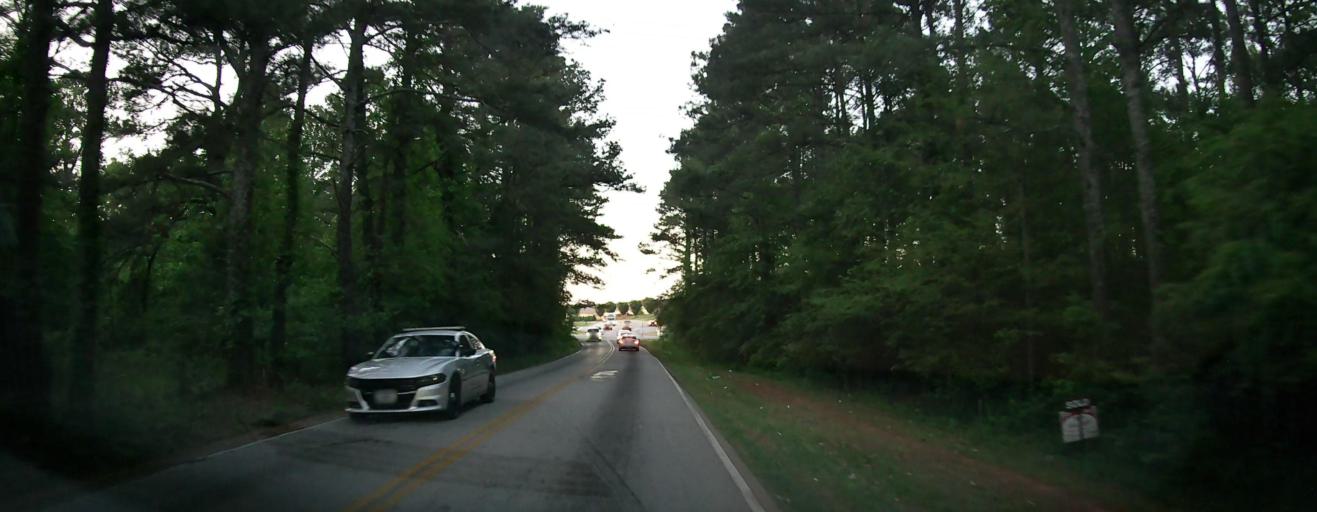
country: US
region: Georgia
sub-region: Henry County
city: McDonough
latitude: 33.4425
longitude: -84.1878
